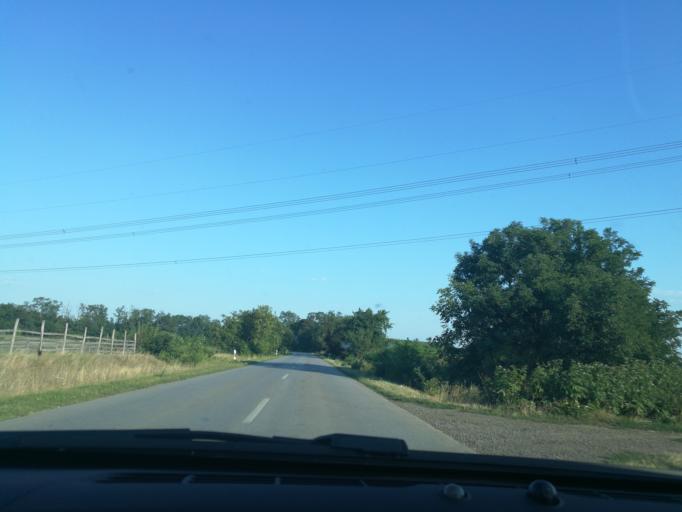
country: HU
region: Szabolcs-Szatmar-Bereg
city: Buj
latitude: 48.0633
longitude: 21.6481
